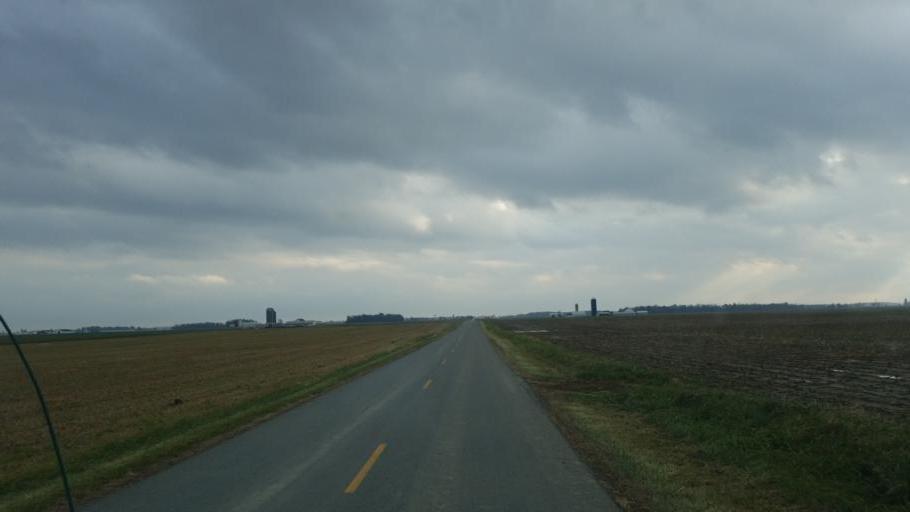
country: US
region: Ohio
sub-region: Mercer County
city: Fort Recovery
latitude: 40.5119
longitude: -84.8028
